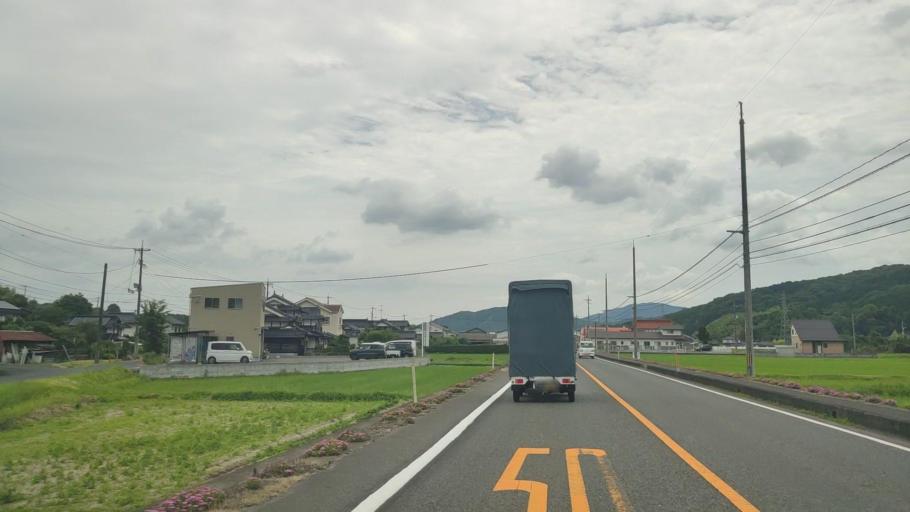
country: JP
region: Okayama
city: Tsuyama
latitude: 35.0550
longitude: 133.9143
